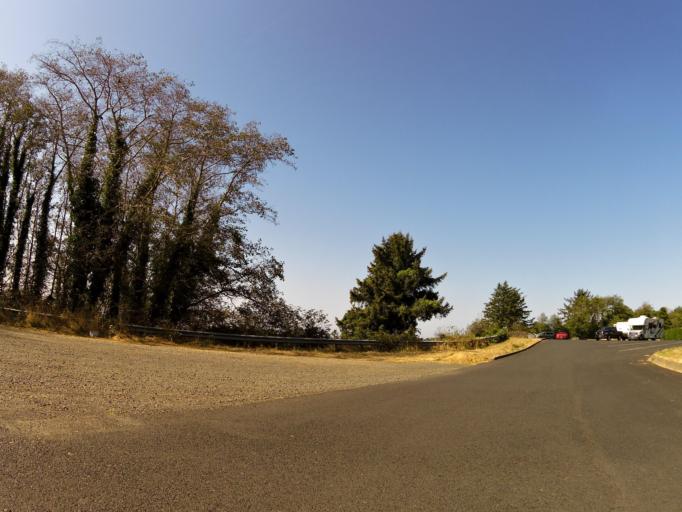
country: US
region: Oregon
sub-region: Tillamook County
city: Pacific City
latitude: 45.1413
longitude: -123.9696
